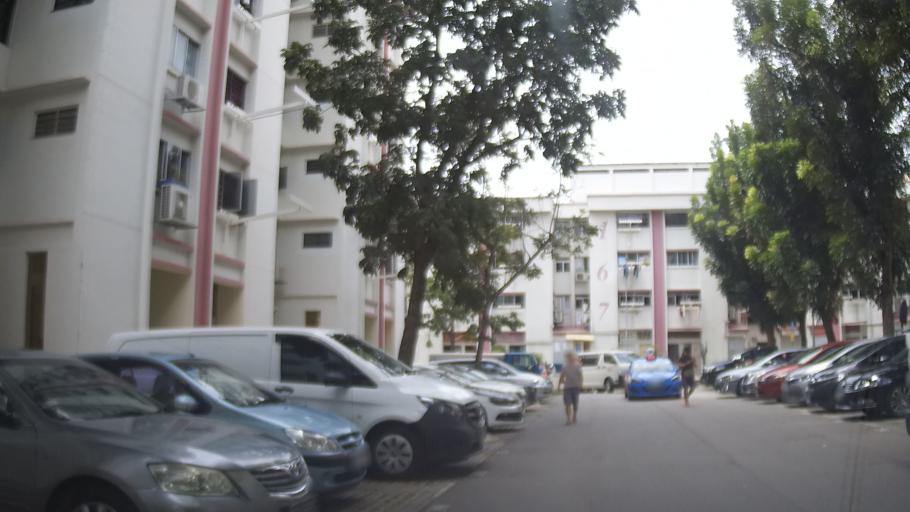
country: MY
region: Johor
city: Johor Bahru
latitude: 1.4337
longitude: 103.7764
